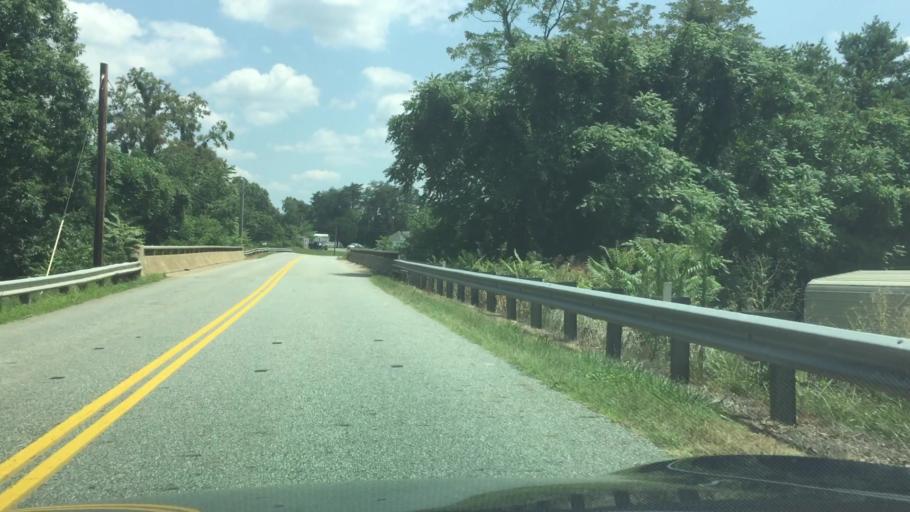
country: US
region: Virginia
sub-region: Campbell County
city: Concord
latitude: 37.3482
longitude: -78.9096
